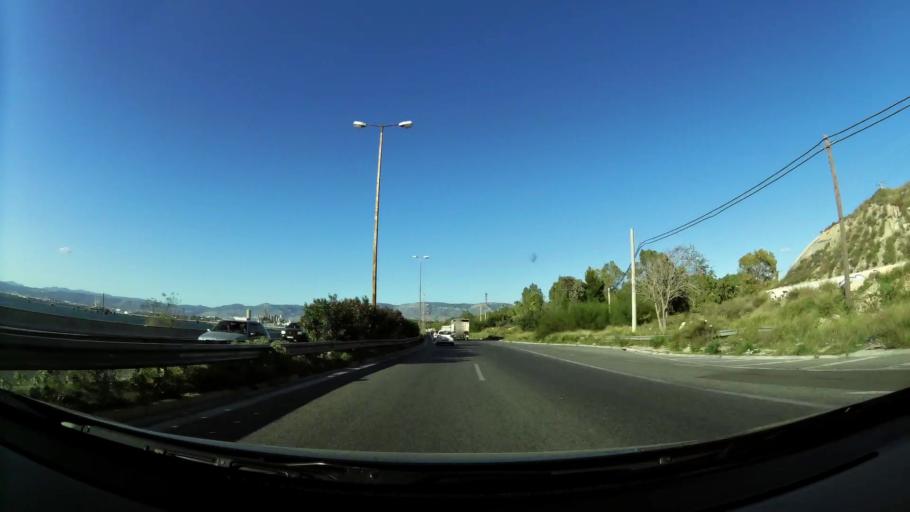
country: GR
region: Attica
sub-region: Nomarchia Athinas
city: Skaramangas
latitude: 38.0174
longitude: 23.5987
